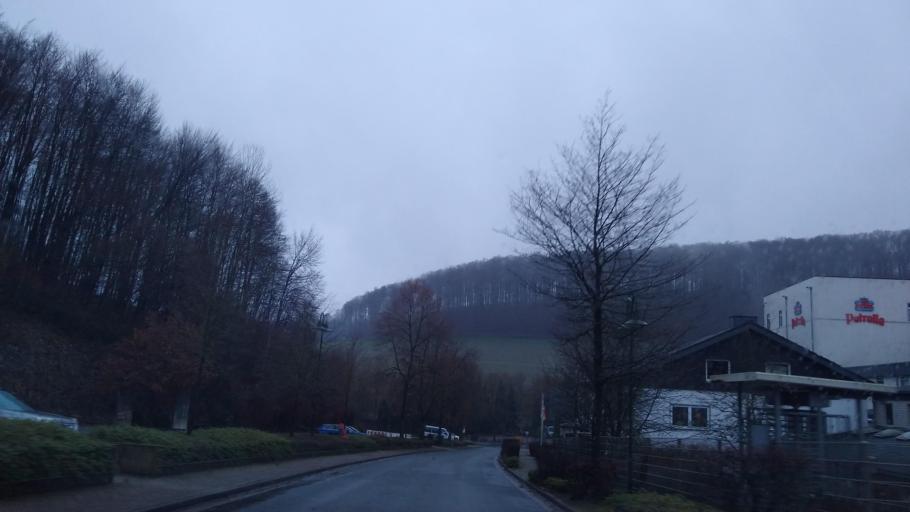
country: DE
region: Lower Saxony
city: Vahlbruch
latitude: 51.9337
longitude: 9.3717
